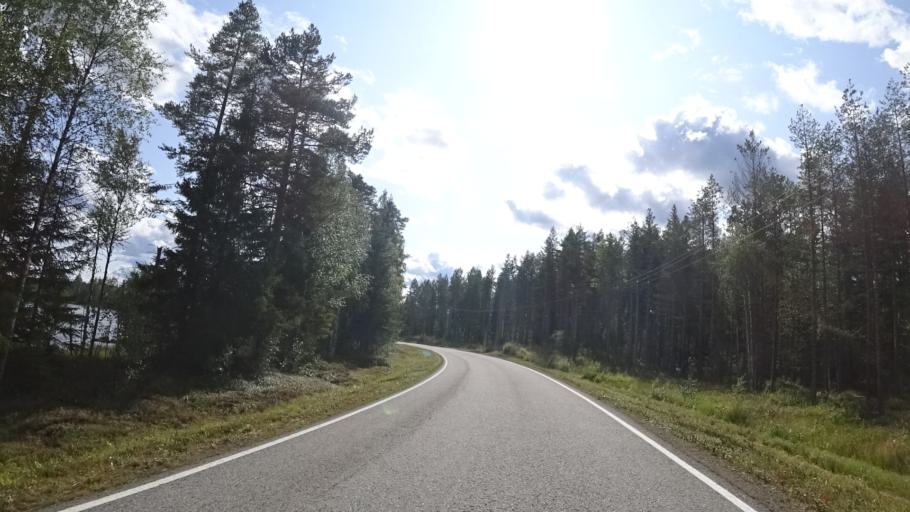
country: RU
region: Republic of Karelia
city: Vyartsilya
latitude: 62.2911
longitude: 30.8078
